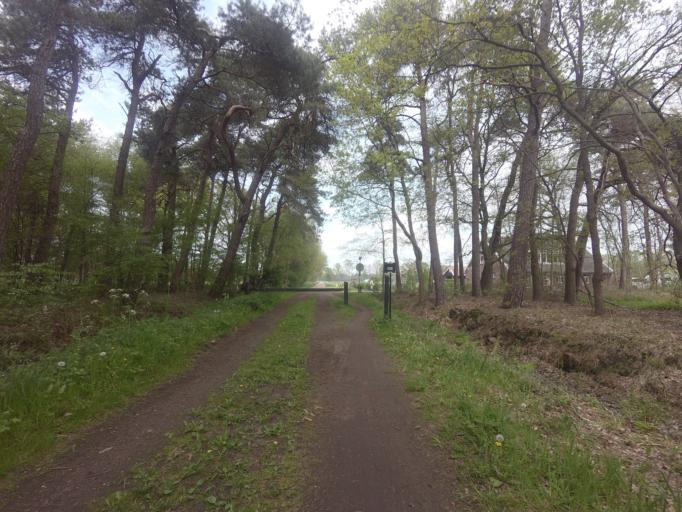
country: NL
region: Overijssel
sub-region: Gemeente Hof van Twente
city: Delden
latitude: 52.2306
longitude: 6.7263
